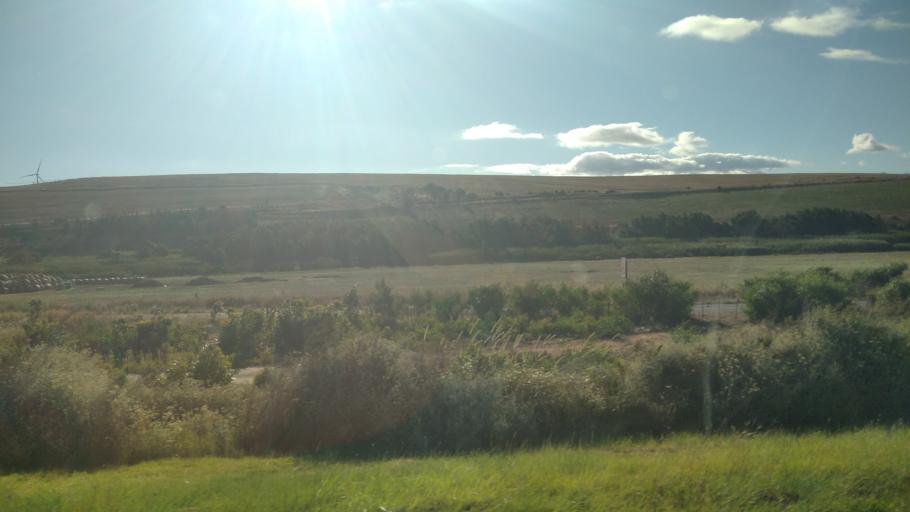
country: ZA
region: Western Cape
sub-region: Overberg District Municipality
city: Caledon
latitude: -34.2132
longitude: 19.3999
